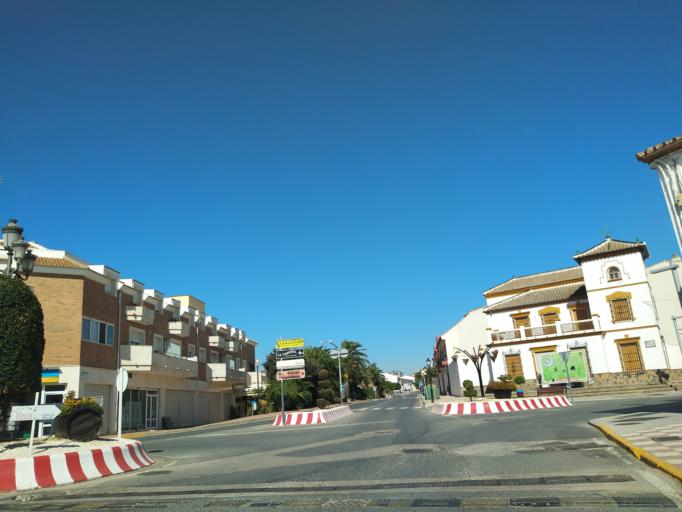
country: ES
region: Andalusia
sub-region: Provincia de Malaga
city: Mollina
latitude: 37.1209
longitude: -4.6591
